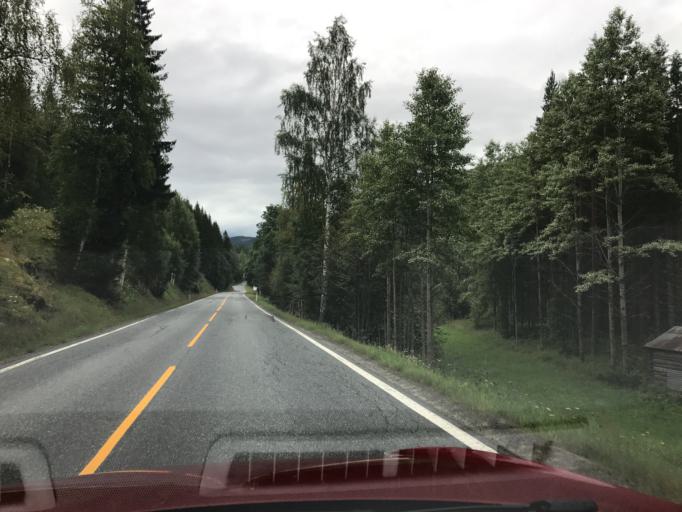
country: NO
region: Buskerud
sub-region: Nore og Uvdal
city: Rodberg
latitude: 60.1574
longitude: 9.0220
